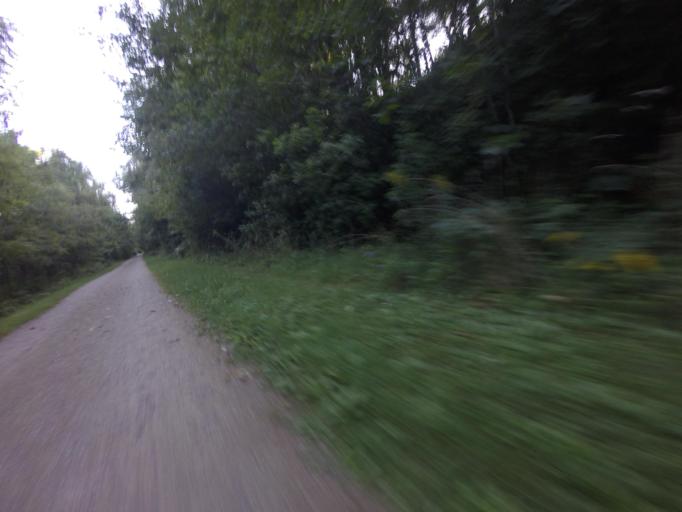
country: CA
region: Ontario
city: Goderich
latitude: 43.7557
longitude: -81.7134
